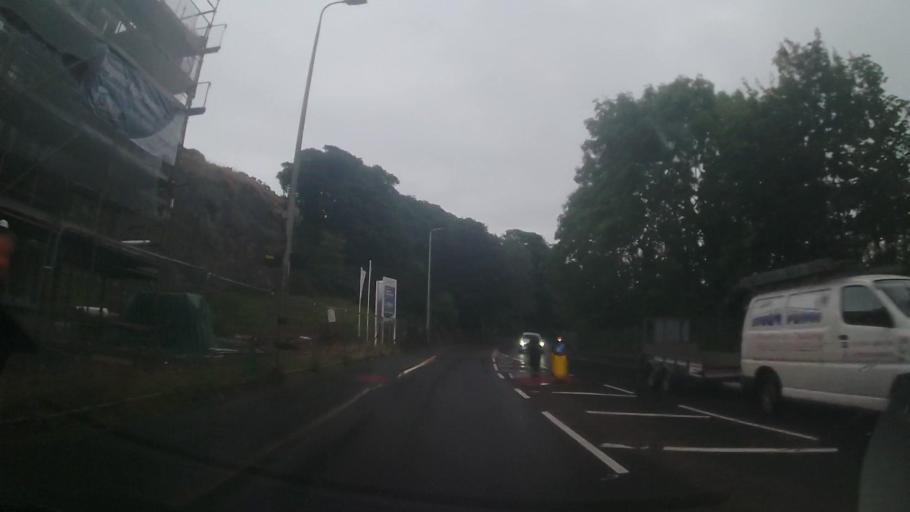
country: GB
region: Scotland
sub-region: North Ayrshire
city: Fairlie
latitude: 55.7615
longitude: -4.8542
